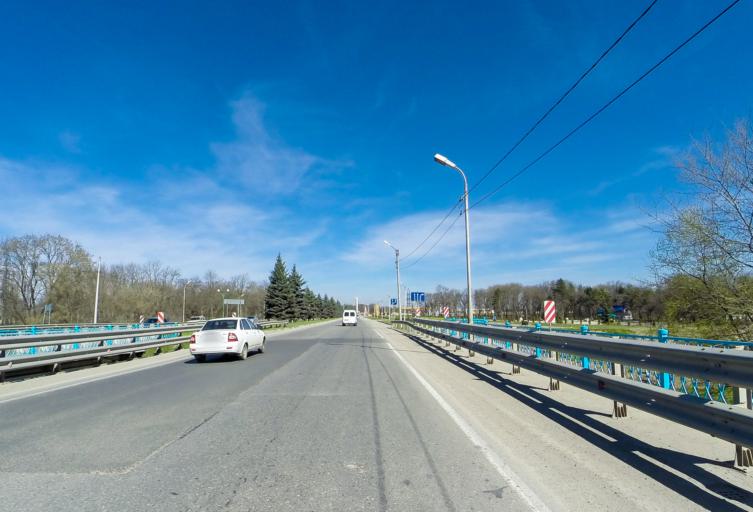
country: RU
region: Kabardino-Balkariya
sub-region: Gorod Nal'chik
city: Nal'chik
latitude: 43.5220
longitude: 43.6121
